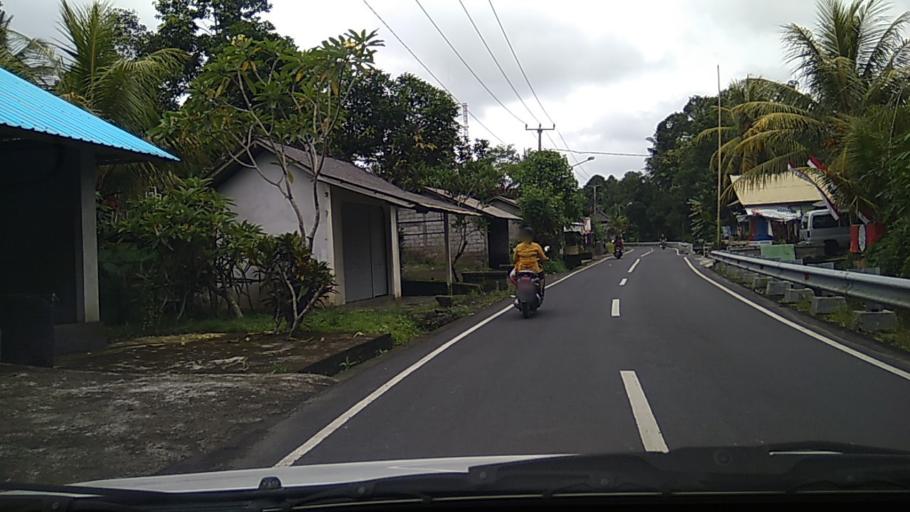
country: ID
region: Bali
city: Basa
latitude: -8.4726
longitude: 115.1870
